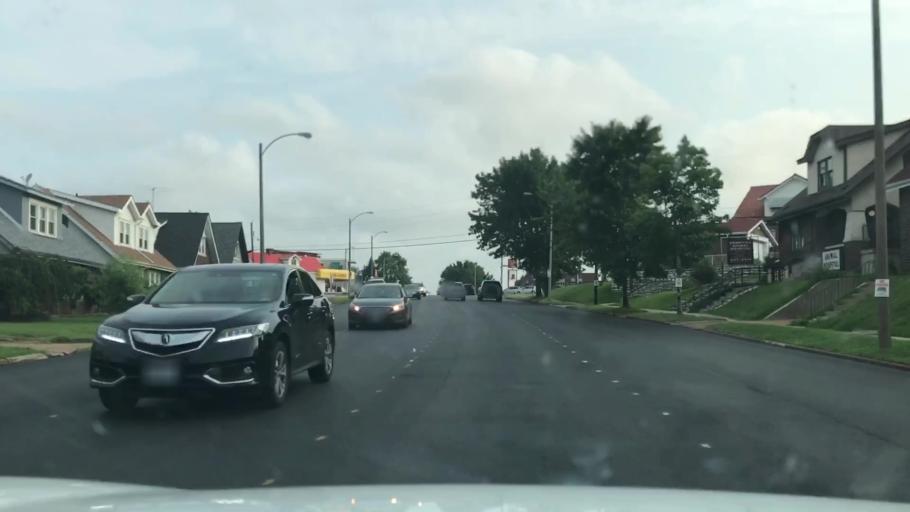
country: US
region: Missouri
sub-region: Saint Louis County
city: Maplewood
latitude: 38.6076
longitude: -90.2887
